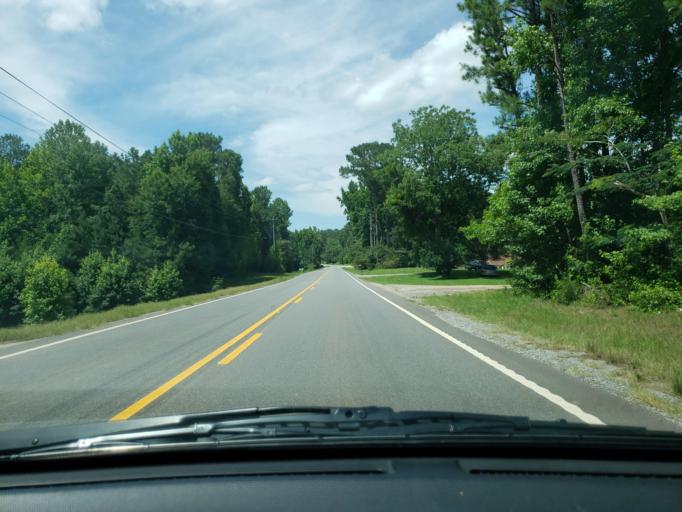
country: US
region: Alabama
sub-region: Elmore County
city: Eclectic
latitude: 32.6612
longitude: -85.9430
